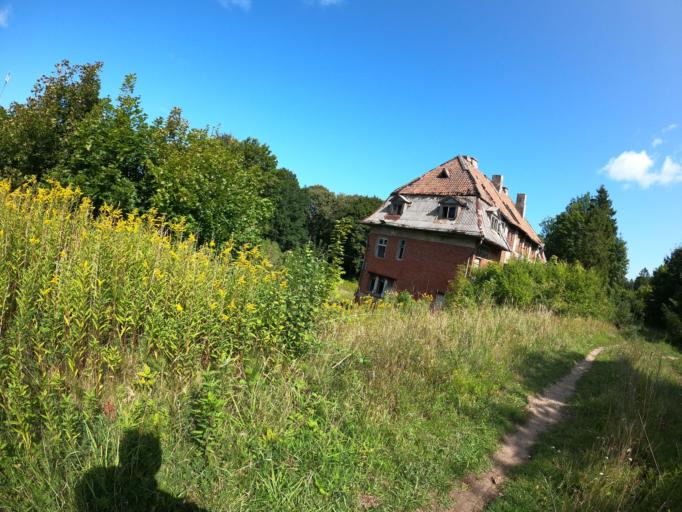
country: RU
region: Kaliningrad
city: Otradnoye
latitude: 54.9375
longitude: 20.1126
